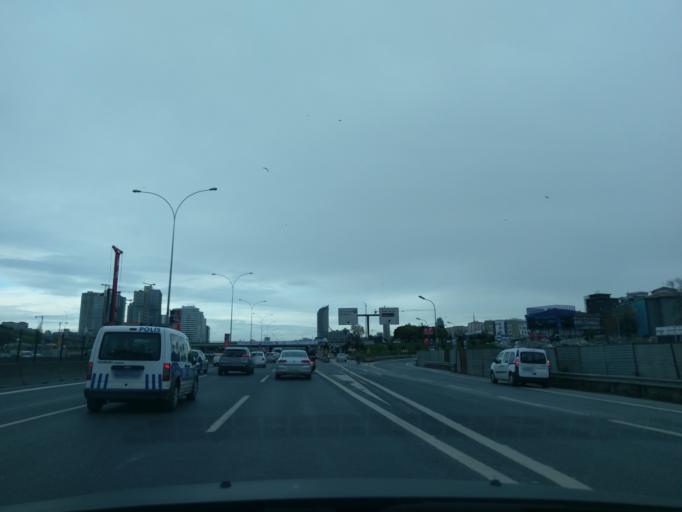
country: TR
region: Istanbul
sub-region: Atasehir
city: Atasehir
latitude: 40.9914
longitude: 29.0764
